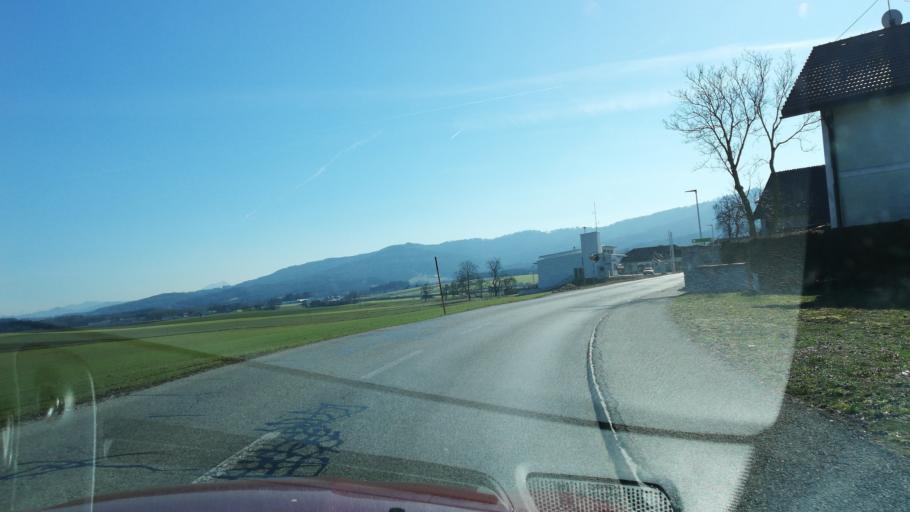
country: AT
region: Upper Austria
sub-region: Politischer Bezirk Vocklabruck
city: Lenzing
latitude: 47.9637
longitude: 13.6330
